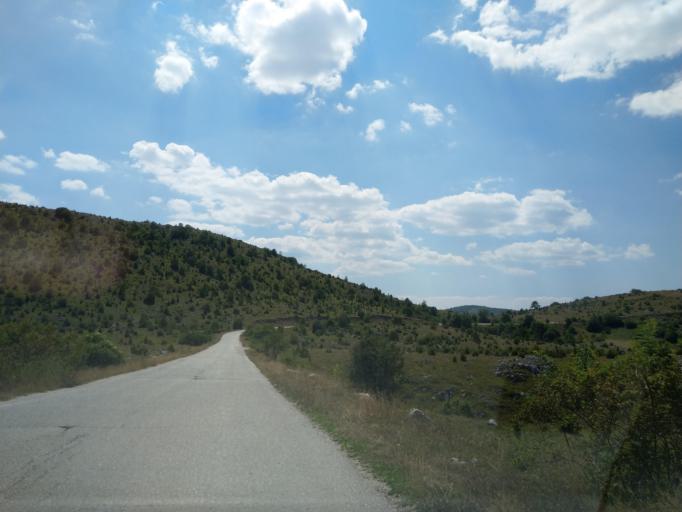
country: RS
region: Central Serbia
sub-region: Zlatiborski Okrug
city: Nova Varos
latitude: 43.4283
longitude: 19.9471
